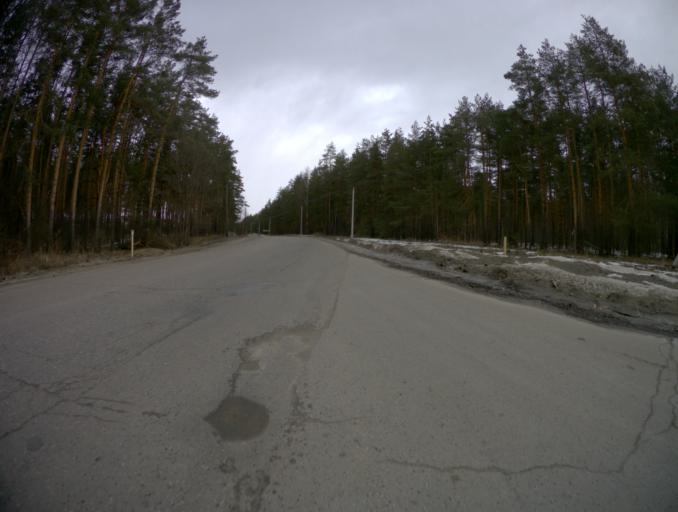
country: RU
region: Vladimir
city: Kommunar
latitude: 56.1325
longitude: 40.4899
